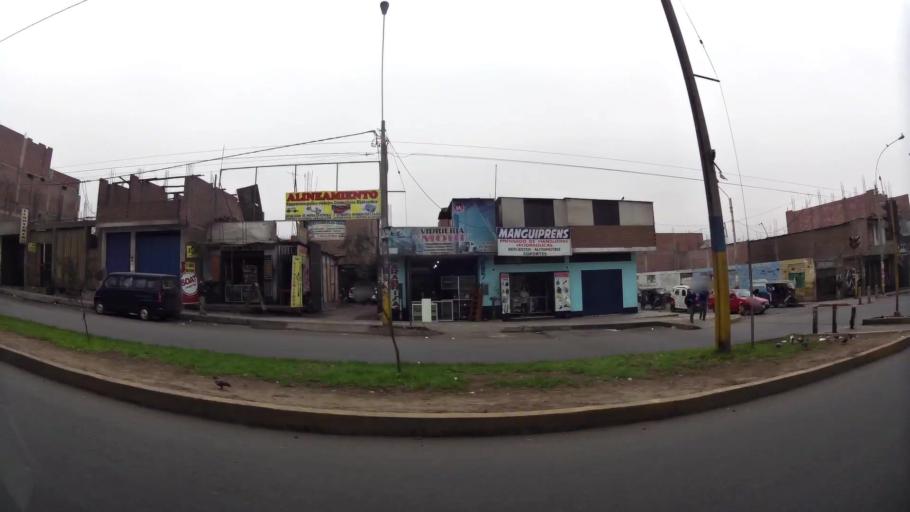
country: PE
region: Lima
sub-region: Lima
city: Independencia
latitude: -11.9610
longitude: -76.9877
